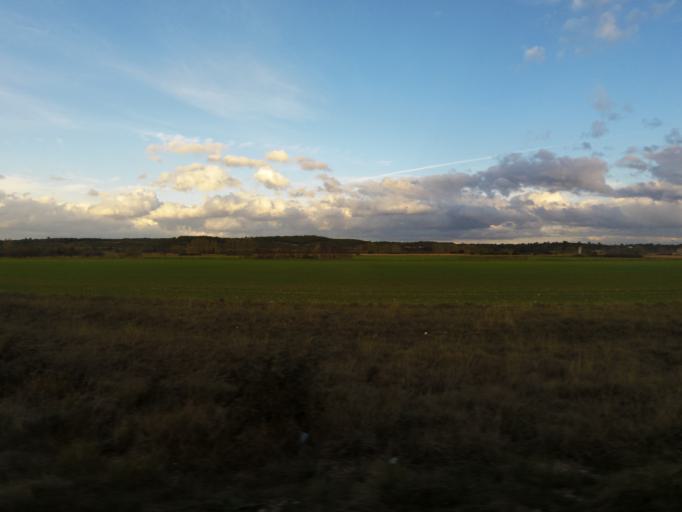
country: FR
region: Languedoc-Roussillon
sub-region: Departement du Gard
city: La Calmette
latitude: 43.8813
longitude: 4.2550
